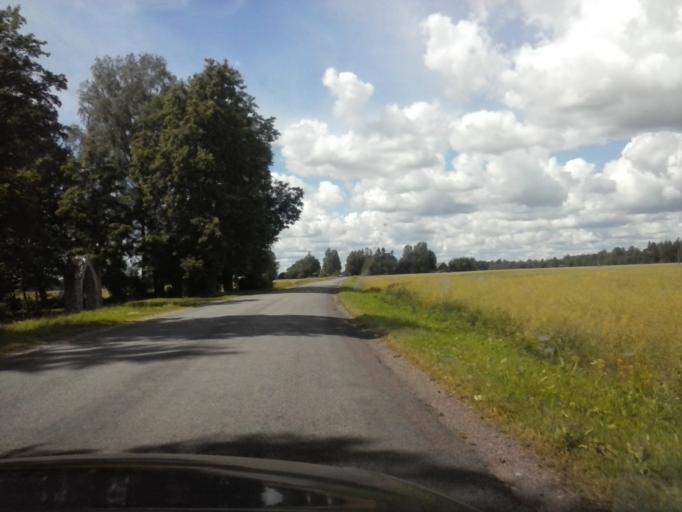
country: EE
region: Laeaene-Virumaa
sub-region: Rakke vald
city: Rakke
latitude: 59.0502
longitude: 26.3726
